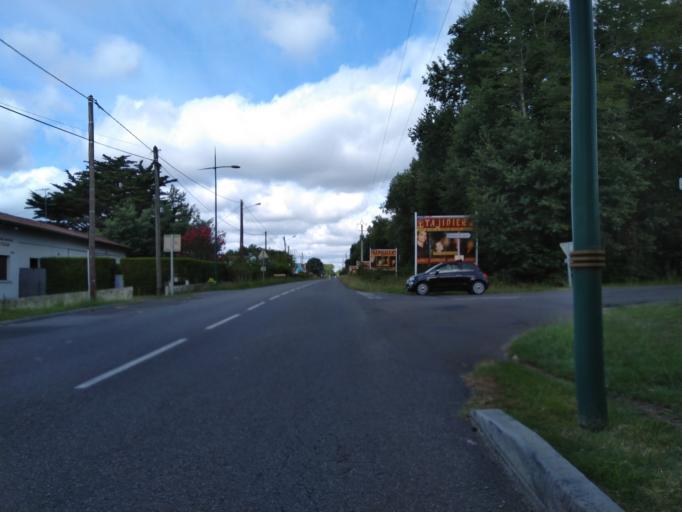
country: FR
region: Aquitaine
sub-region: Departement des Landes
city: Mees
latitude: 43.7303
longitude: -1.0934
